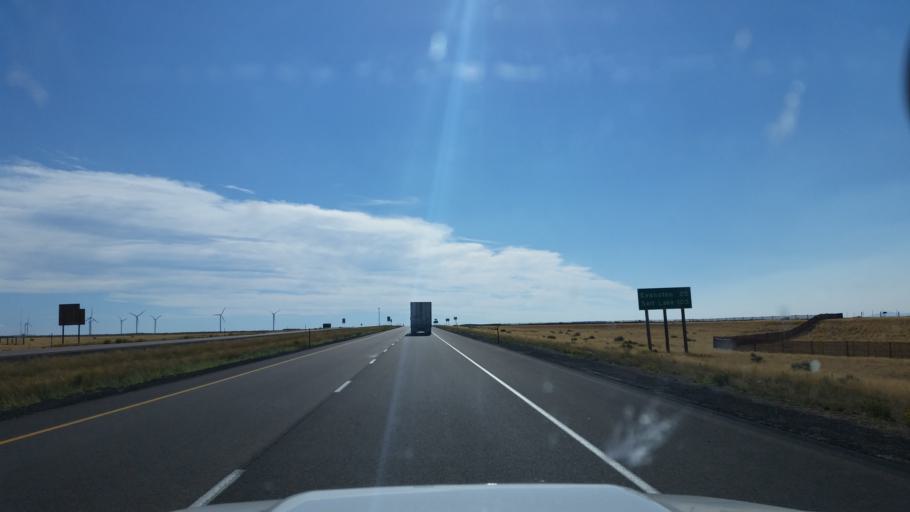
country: US
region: Wyoming
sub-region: Uinta County
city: Mountain View
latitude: 41.3075
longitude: -110.5247
